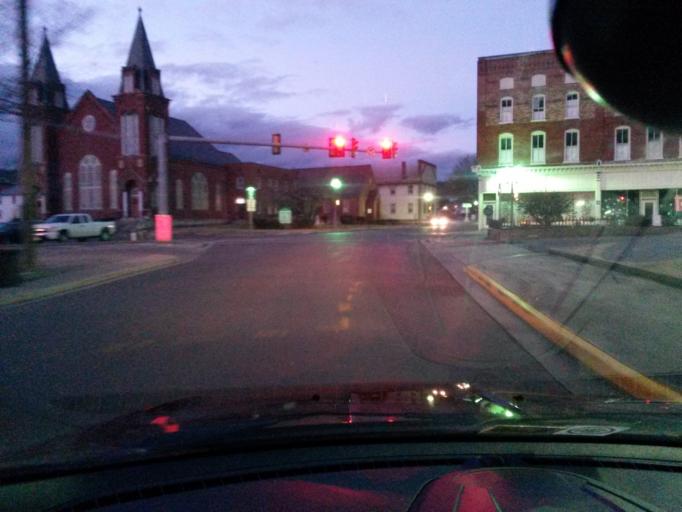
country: US
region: Virginia
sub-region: Alleghany County
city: Clifton Forge
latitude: 37.8160
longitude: -79.8260
